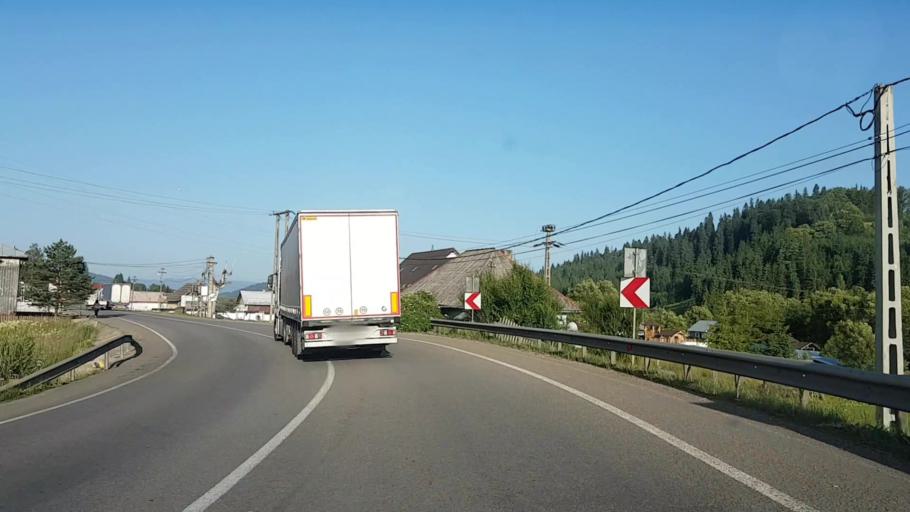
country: RO
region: Suceava
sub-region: Comuna Cosna
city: Cosna
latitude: 47.3609
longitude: 25.1963
